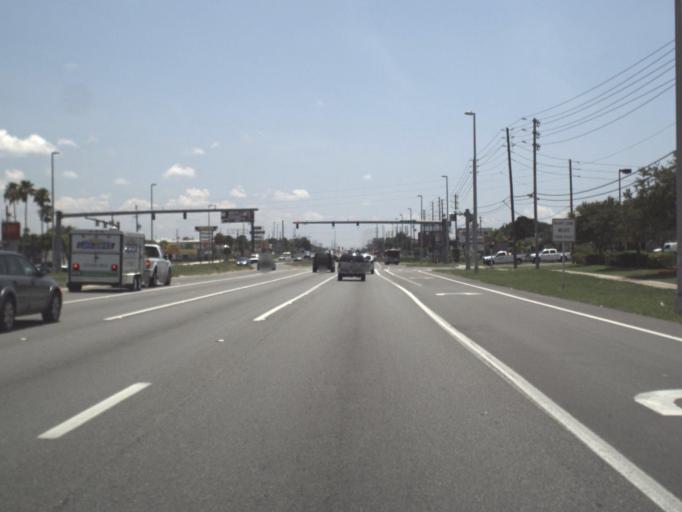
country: US
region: Florida
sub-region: Pasco County
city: Holiday
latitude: 28.1782
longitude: -82.7406
